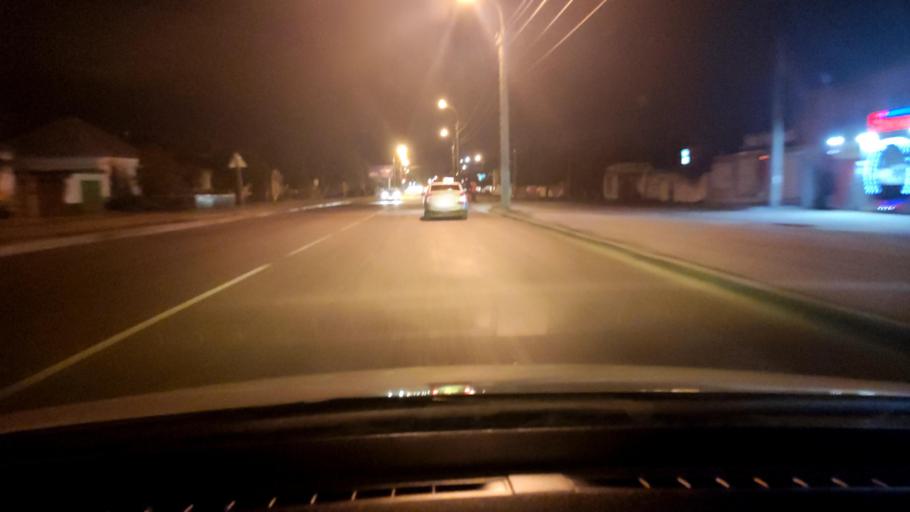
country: RU
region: Voronezj
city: Voronezh
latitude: 51.6418
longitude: 39.1569
